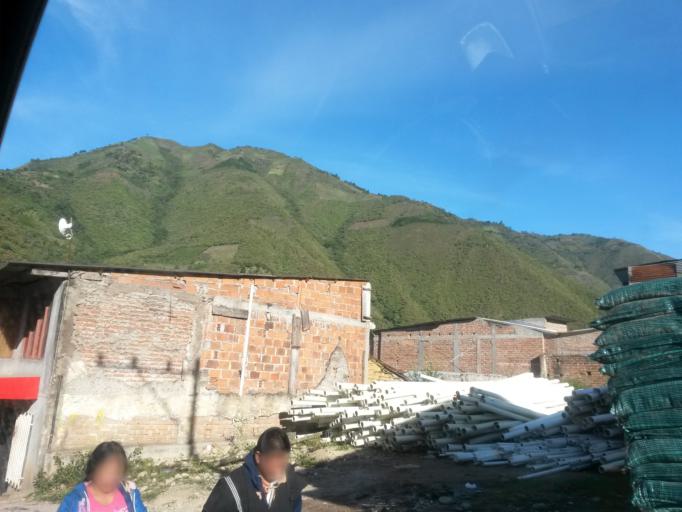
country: CO
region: Cauca
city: Belalcazar
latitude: 2.6456
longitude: -75.9719
